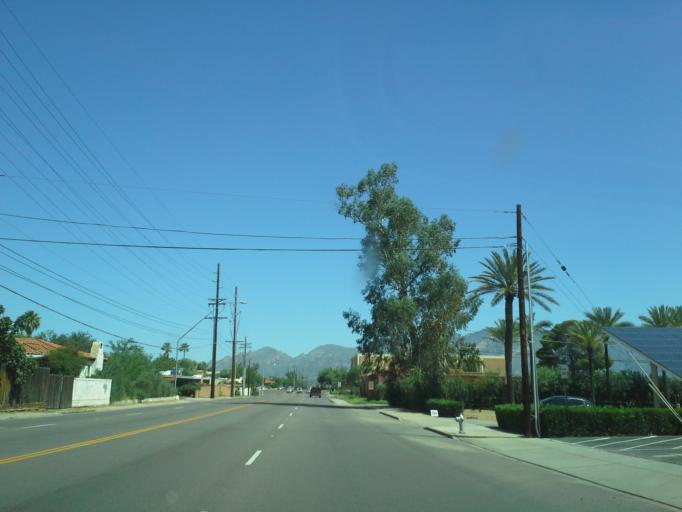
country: US
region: Arizona
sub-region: Pima County
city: Tucson
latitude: 32.2331
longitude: -110.9267
